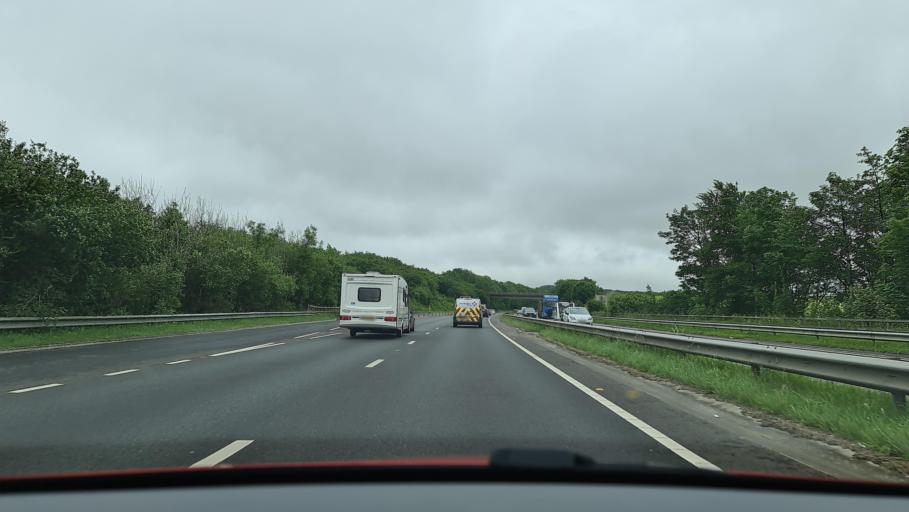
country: GB
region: England
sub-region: Cornwall
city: Bodmin
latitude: 50.4467
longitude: -4.7011
